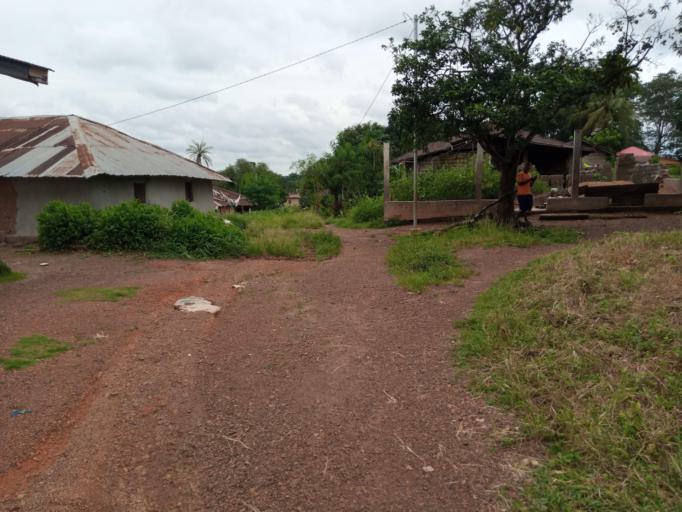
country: SL
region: Southern Province
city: Largo
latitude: 8.2034
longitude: -12.0588
